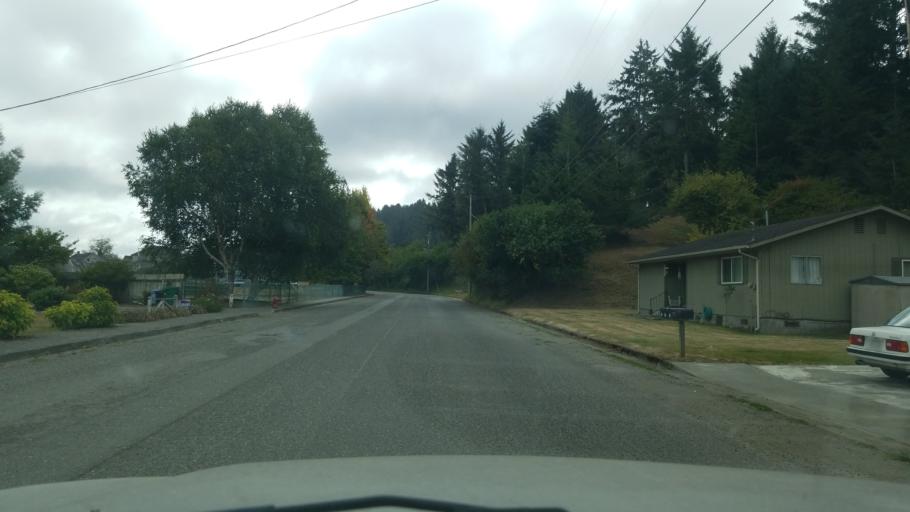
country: US
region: California
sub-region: Humboldt County
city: Ferndale
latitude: 40.5774
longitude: -124.2690
